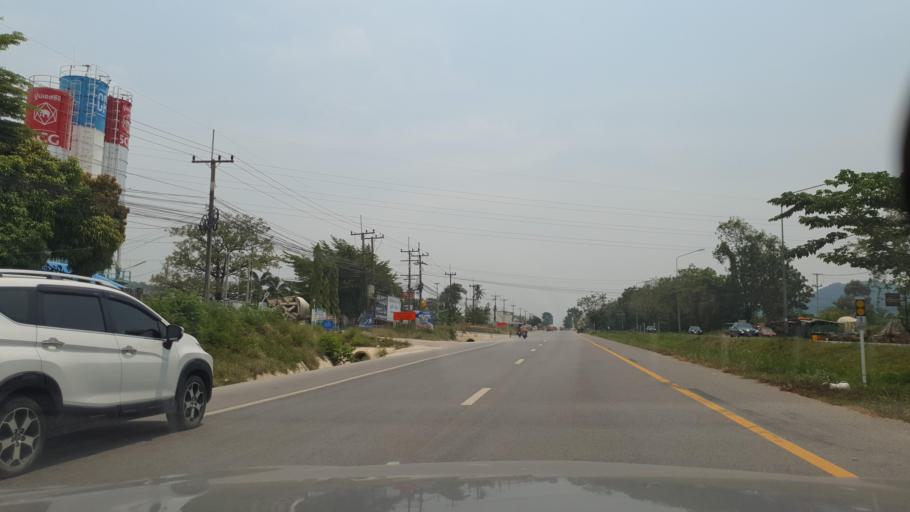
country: TH
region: Chon Buri
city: Sattahip
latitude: 12.7305
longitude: 100.9044
